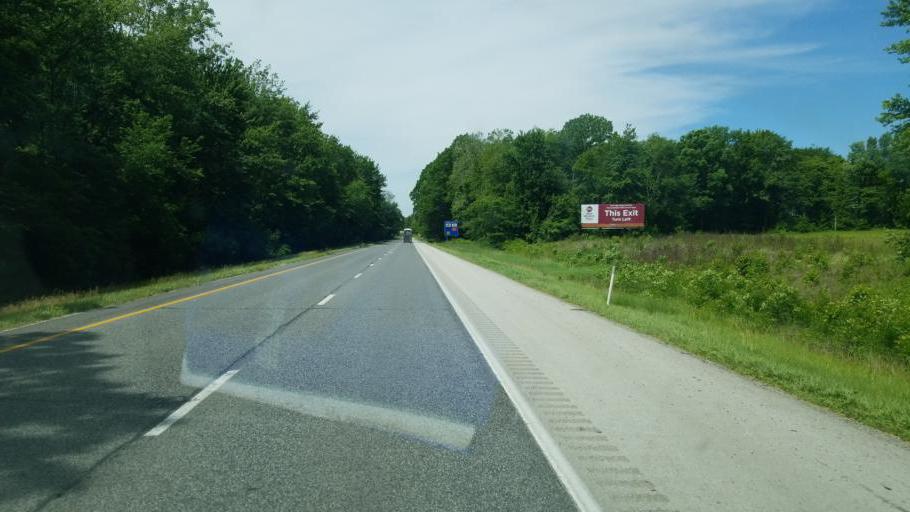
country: US
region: Indiana
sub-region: Clay County
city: Brazil
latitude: 39.4578
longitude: -87.0911
